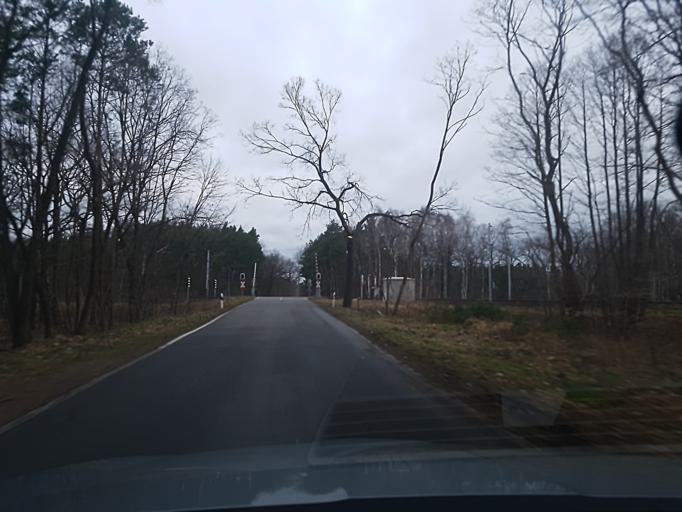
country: DE
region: Brandenburg
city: Schilda
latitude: 51.5863
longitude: 13.3172
